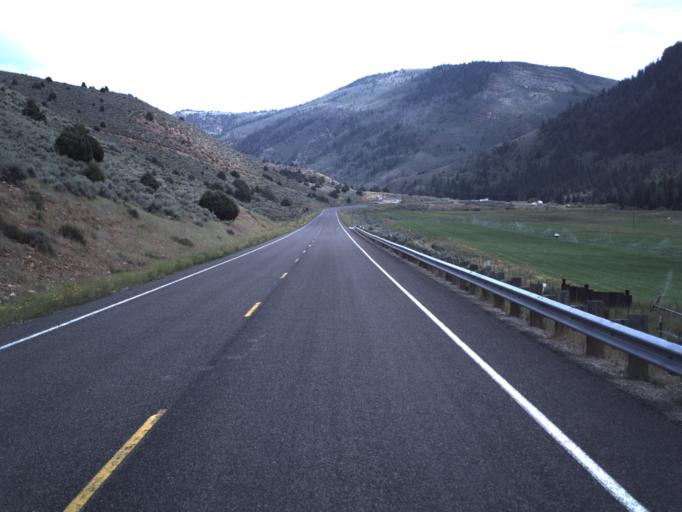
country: US
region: Utah
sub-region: Summit County
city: Francis
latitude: 40.4531
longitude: -110.8787
